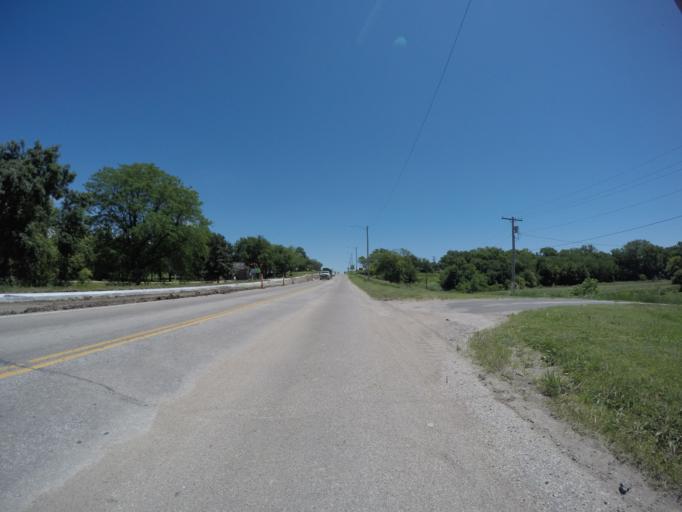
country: US
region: Kansas
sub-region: Jewell County
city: Mankato
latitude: 39.7847
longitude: -98.2142
